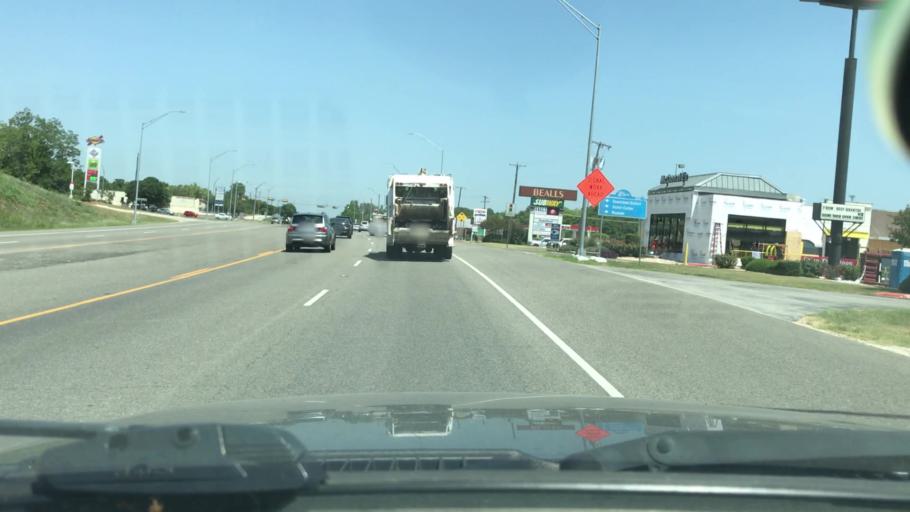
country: US
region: Texas
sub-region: Bastrop County
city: Elgin
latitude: 30.3380
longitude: -97.3729
